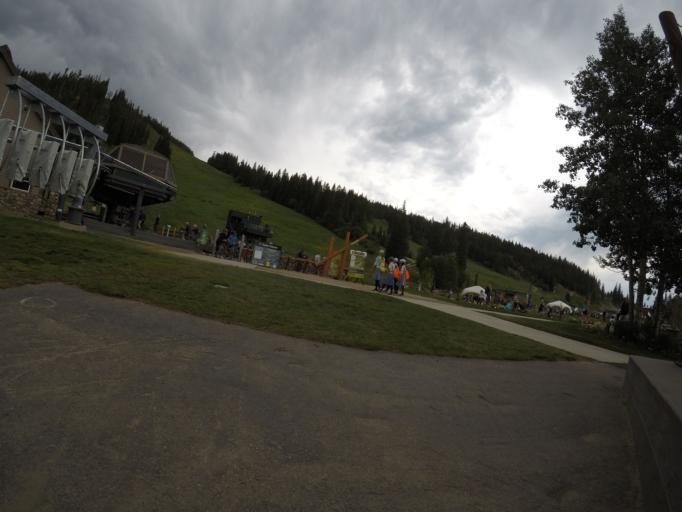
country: US
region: Colorado
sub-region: Grand County
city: Fraser
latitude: 39.8861
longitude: -105.7629
